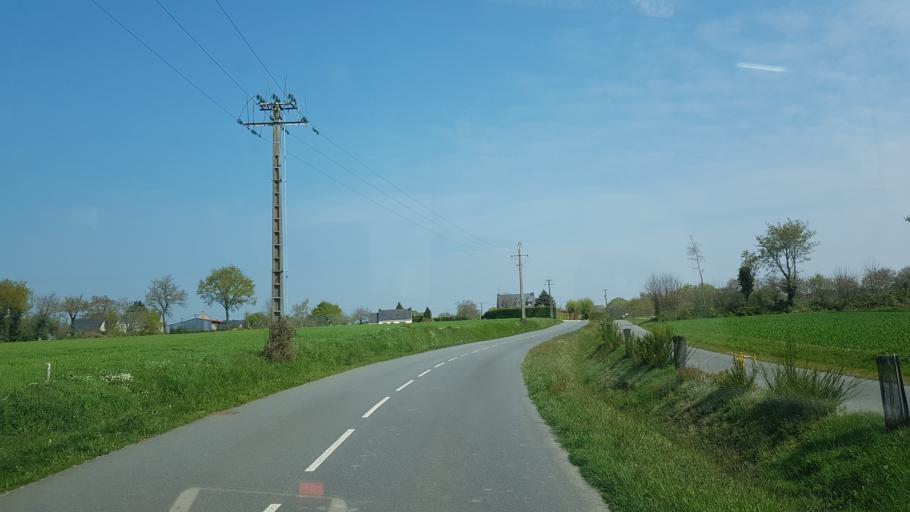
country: FR
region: Brittany
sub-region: Departement du Morbihan
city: Noyal-Muzillac
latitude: 47.5868
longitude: -2.4060
